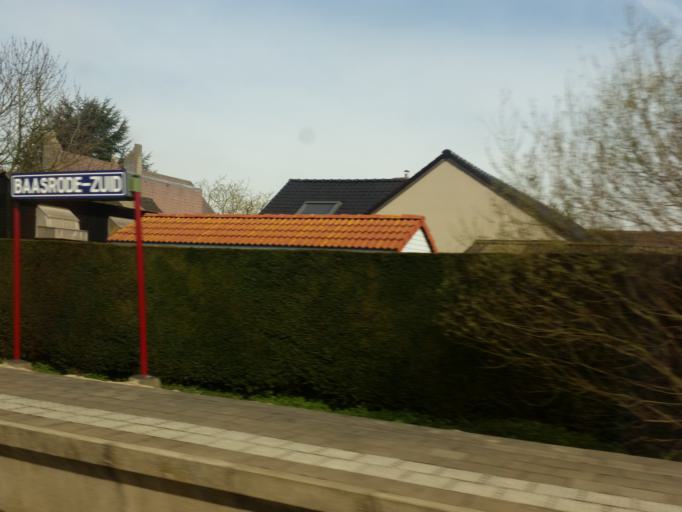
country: BE
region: Flanders
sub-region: Provincie Oost-Vlaanderen
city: Lebbeke
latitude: 51.0192
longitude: 4.1555
